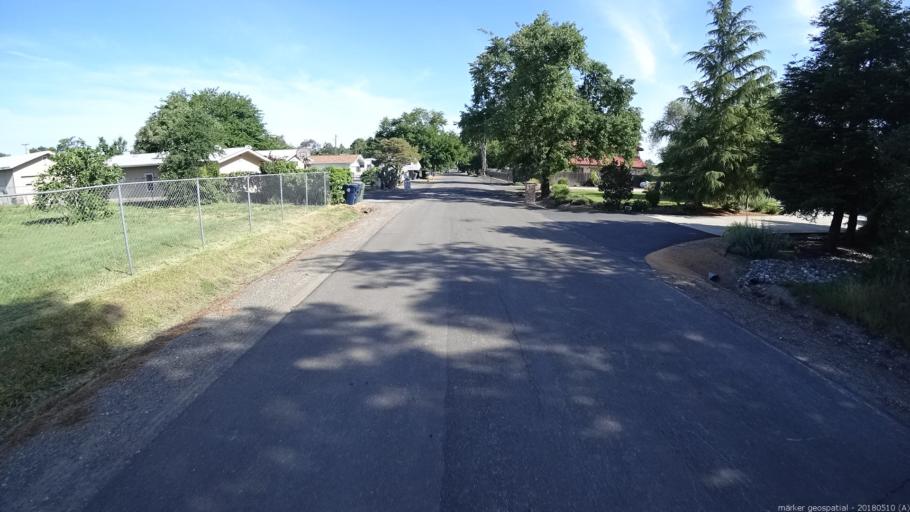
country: US
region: California
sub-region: Sacramento County
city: Rio Linda
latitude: 38.6581
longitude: -121.4780
